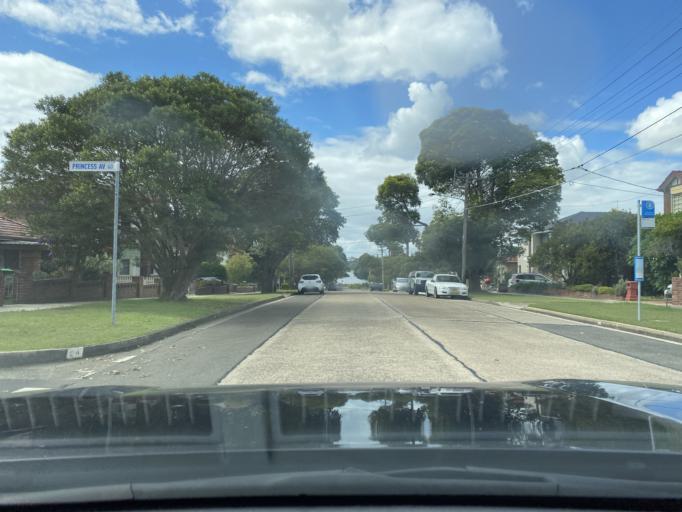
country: AU
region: New South Wales
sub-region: Canada Bay
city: Wareemba
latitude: -33.8657
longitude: 151.1433
